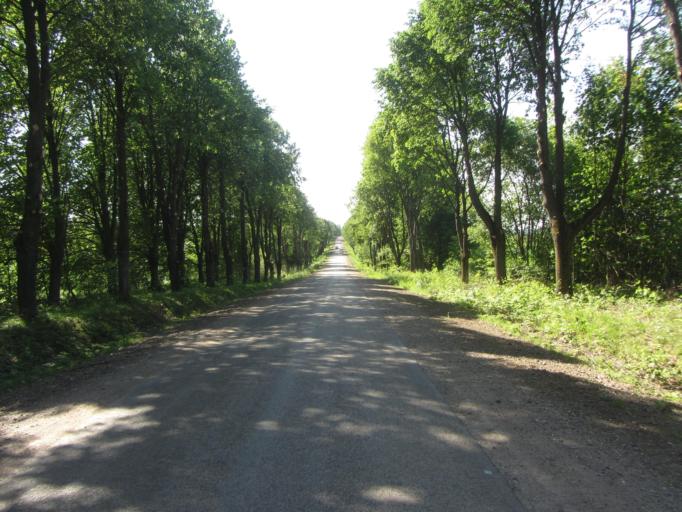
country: LT
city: Jieznas
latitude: 54.5632
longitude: 24.1587
